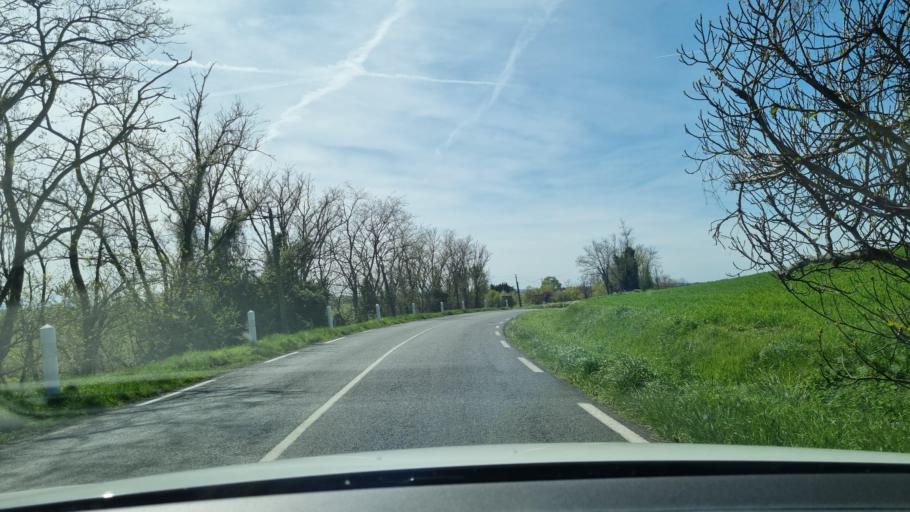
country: FR
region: Midi-Pyrenees
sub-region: Departement de la Haute-Garonne
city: Sainte-Foy-de-Peyrolieres
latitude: 43.4869
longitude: 1.0483
